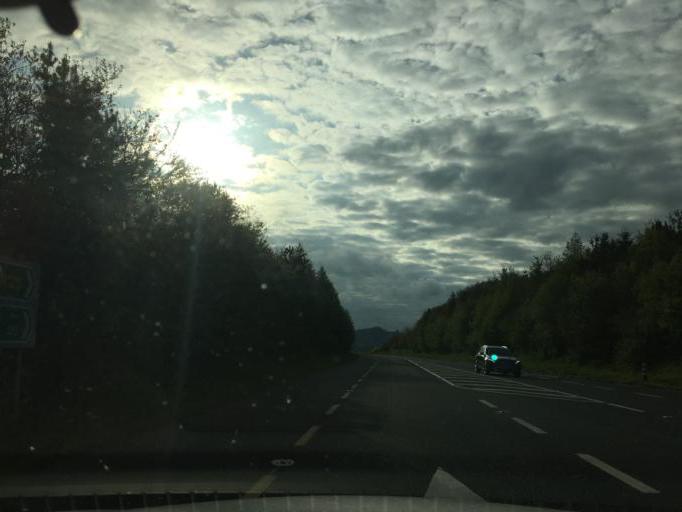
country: IE
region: Leinster
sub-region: Loch Garman
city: Enniscorthy
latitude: 52.3609
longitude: -6.7153
